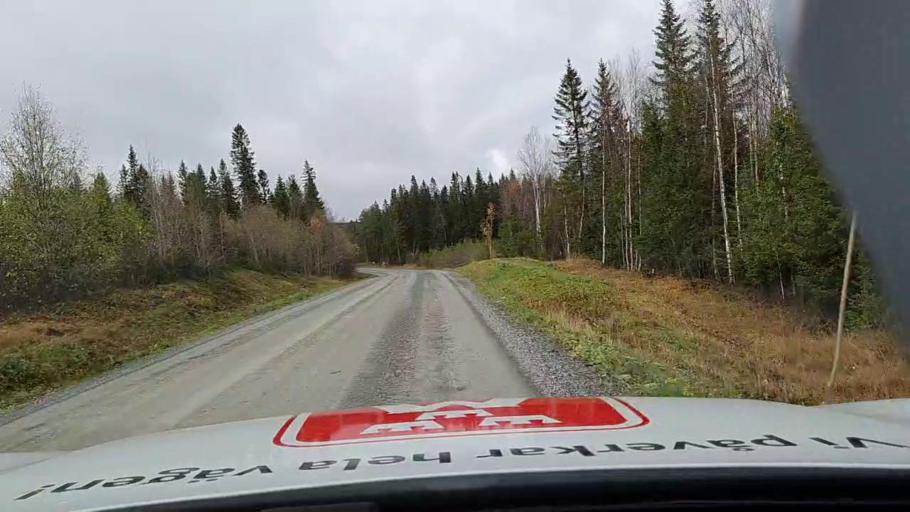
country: SE
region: Jaemtland
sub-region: Bergs Kommun
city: Hoverberg
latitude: 63.0005
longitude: 14.1422
